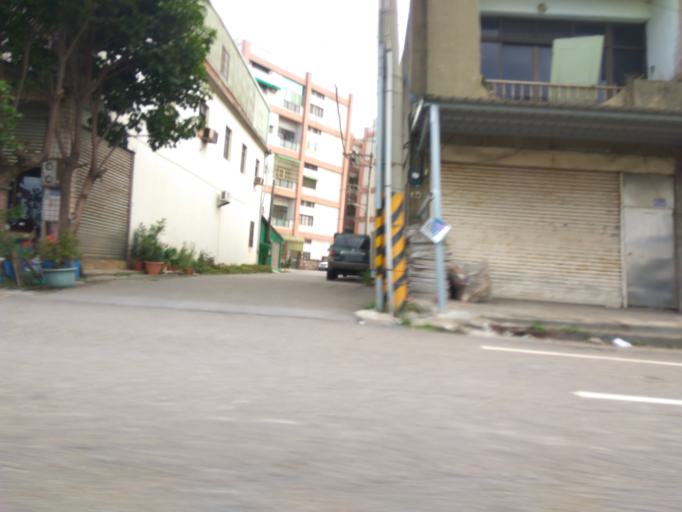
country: TW
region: Taiwan
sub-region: Hsinchu
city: Zhubei
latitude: 24.9853
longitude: 121.0274
